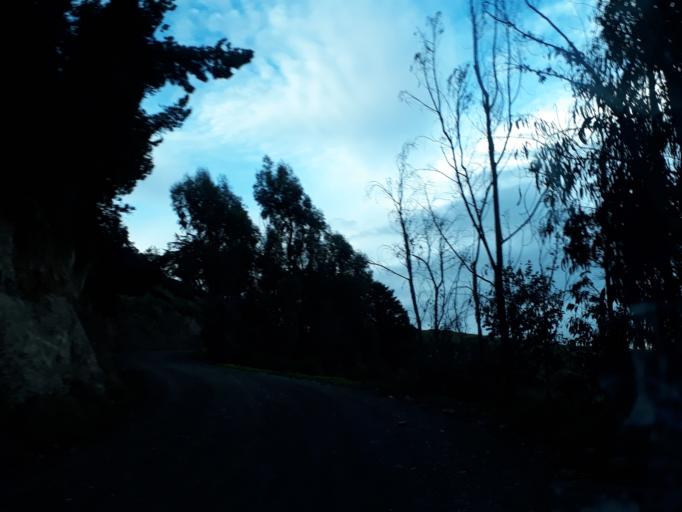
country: CO
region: Cundinamarca
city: Carmen de Carupa
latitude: 5.3461
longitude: -73.9061
